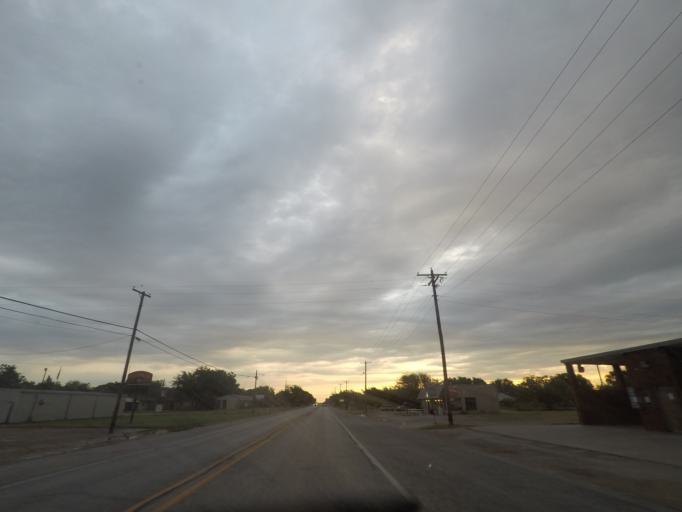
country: US
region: Texas
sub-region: Clay County
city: Henrietta
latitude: 34.0132
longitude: -98.2326
